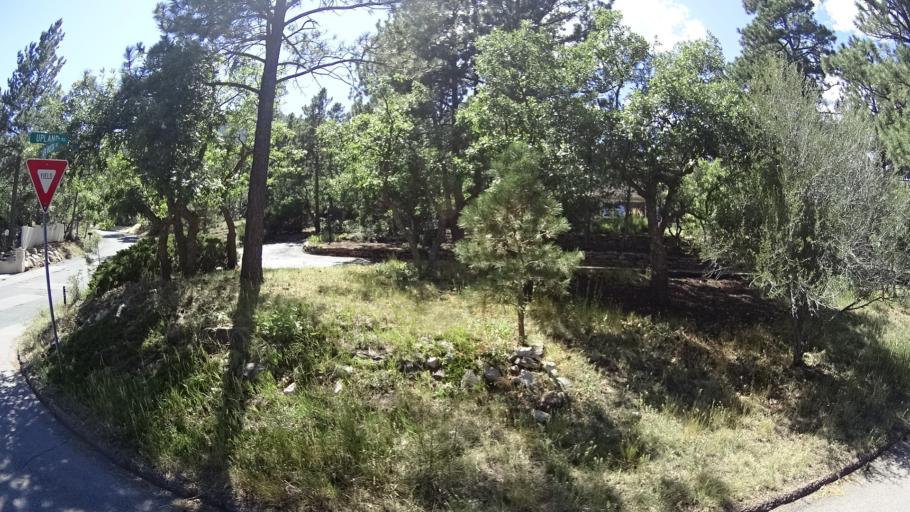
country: US
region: Colorado
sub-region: El Paso County
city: Colorado Springs
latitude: 38.7844
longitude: -104.8625
